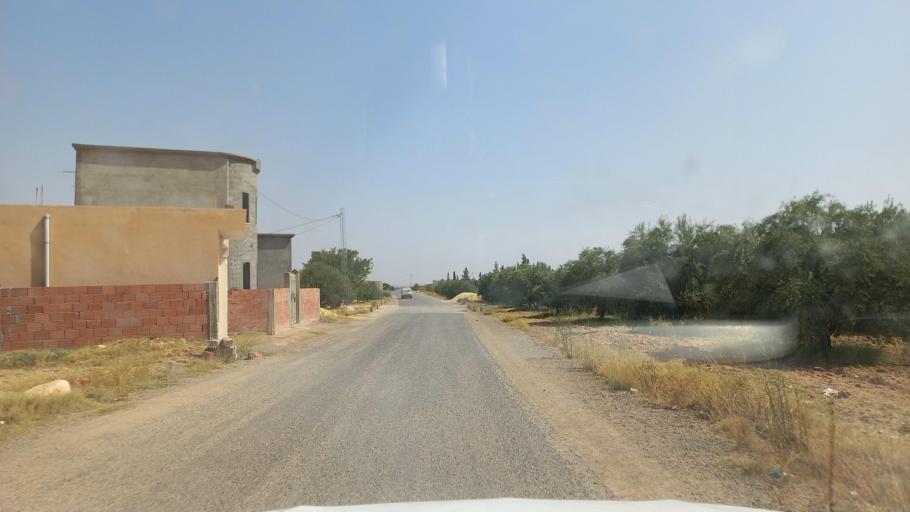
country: TN
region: Al Qasrayn
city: Kasserine
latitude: 35.2462
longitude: 9.0242
